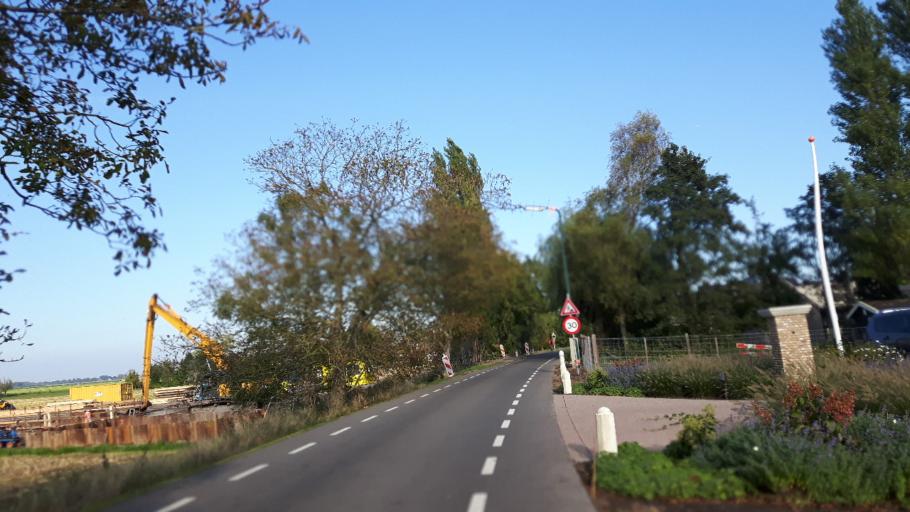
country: NL
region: Utrecht
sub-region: Gemeente Oudewater
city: Oudewater
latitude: 52.0272
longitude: 4.8982
